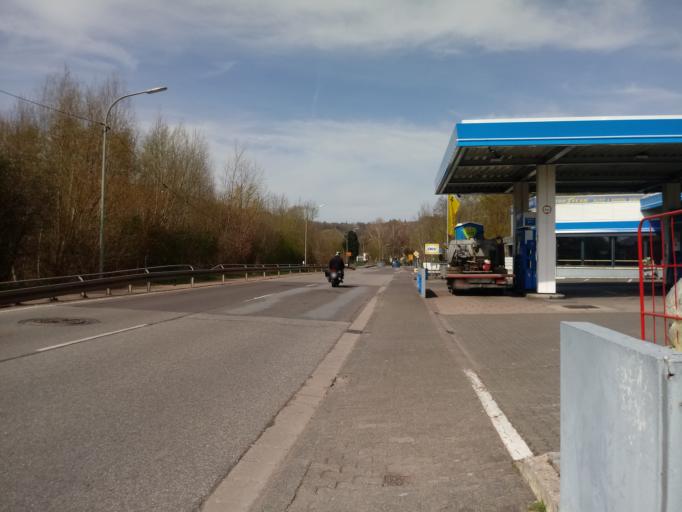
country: DE
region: Saarland
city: Uberherrn
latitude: 49.2481
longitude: 6.6972
